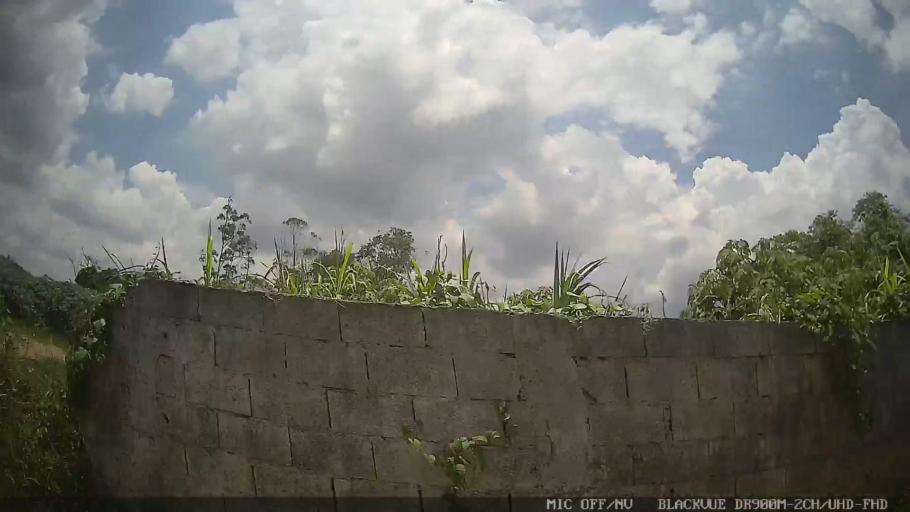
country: BR
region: Sao Paulo
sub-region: Ferraz De Vasconcelos
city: Ferraz de Vasconcelos
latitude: -23.5826
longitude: -46.3533
